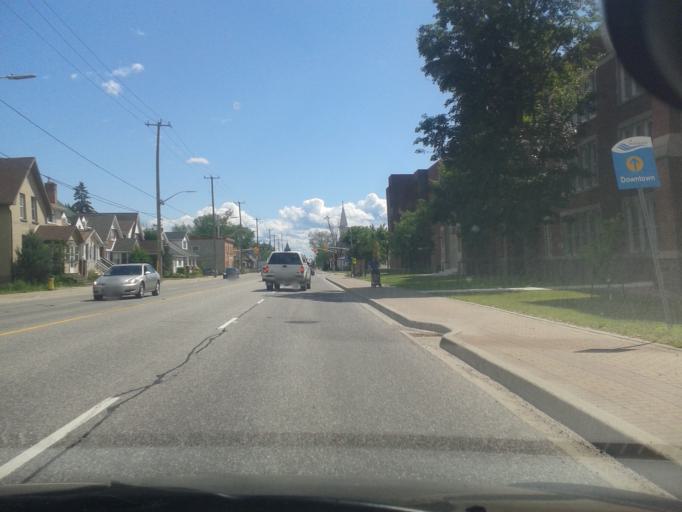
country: CA
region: Ontario
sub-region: Nipissing District
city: North Bay
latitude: 46.3194
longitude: -79.4662
